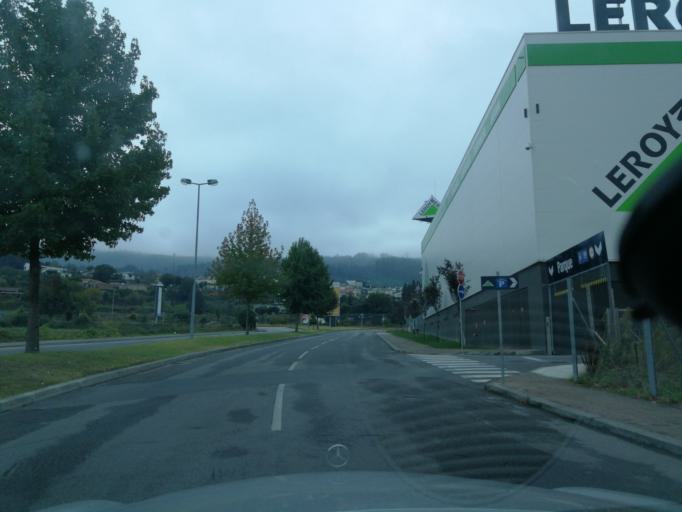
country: PT
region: Braga
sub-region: Braga
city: Braga
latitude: 41.5478
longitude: -8.3989
